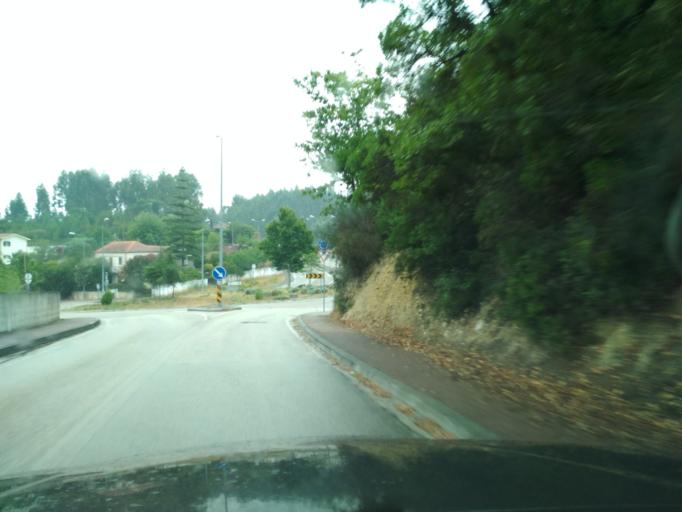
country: PT
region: Coimbra
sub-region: Coimbra
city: Coimbra
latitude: 40.1775
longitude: -8.4524
